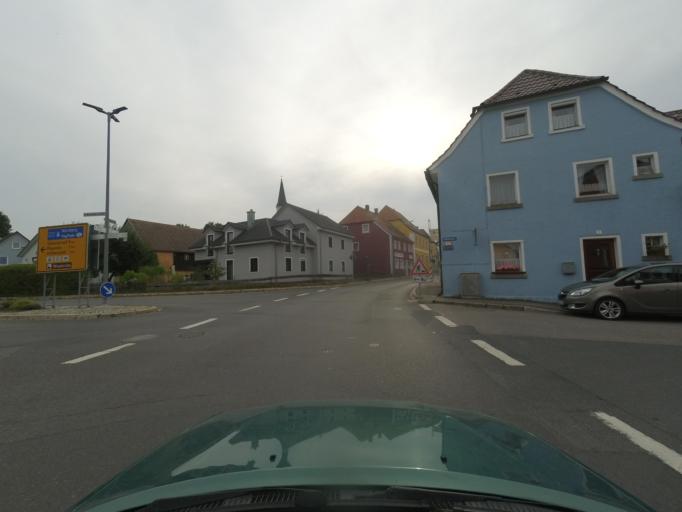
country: DE
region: Bavaria
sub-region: Upper Palatinate
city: Moosbach
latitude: 49.5915
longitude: 12.4070
